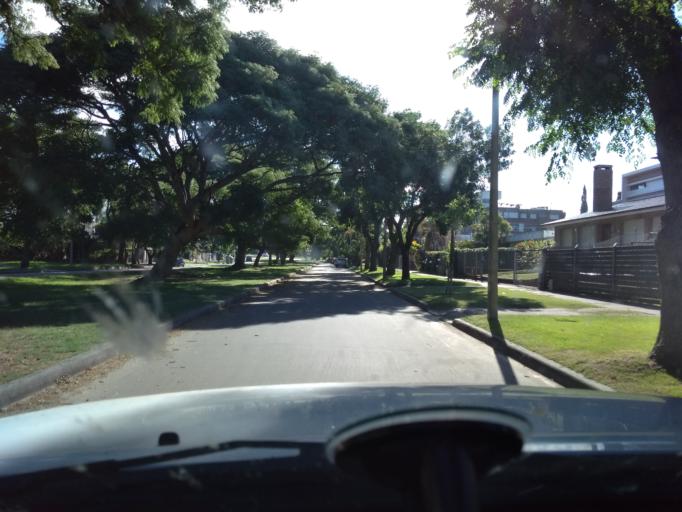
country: UY
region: Canelones
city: Paso de Carrasco
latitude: -34.8888
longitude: -56.0704
